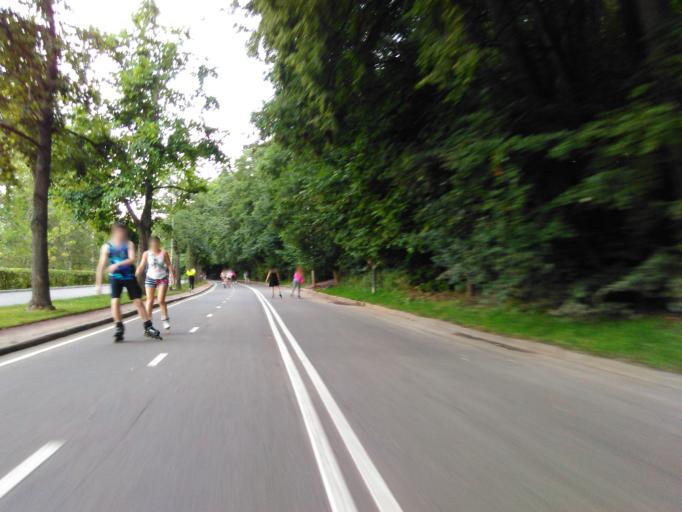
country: RU
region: Moscow
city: Vorob'yovo
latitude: 55.7161
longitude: 37.5403
